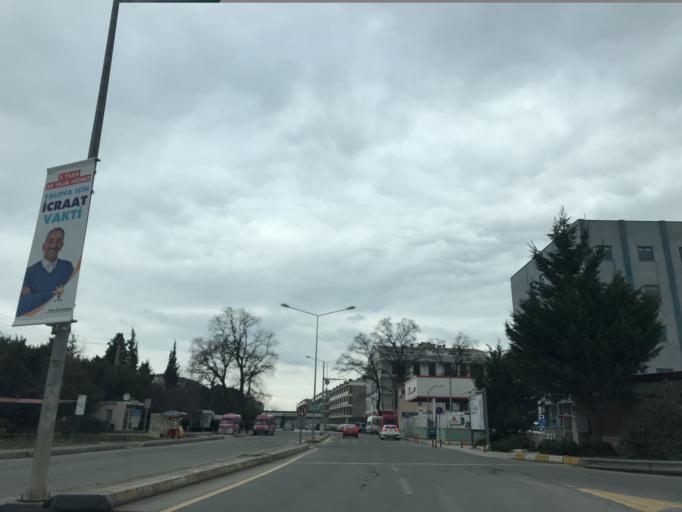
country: TR
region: Yalova
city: Ciftlikkoy
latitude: 40.6624
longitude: 29.3066
